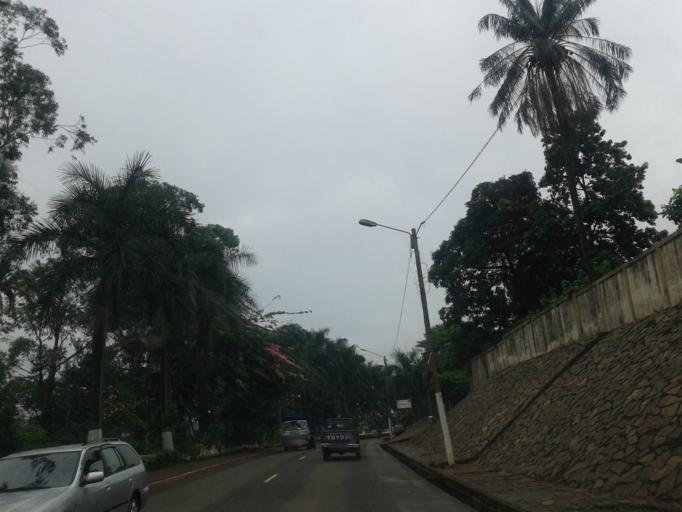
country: CM
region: Centre
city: Yaounde
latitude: 3.8747
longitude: 11.5140
